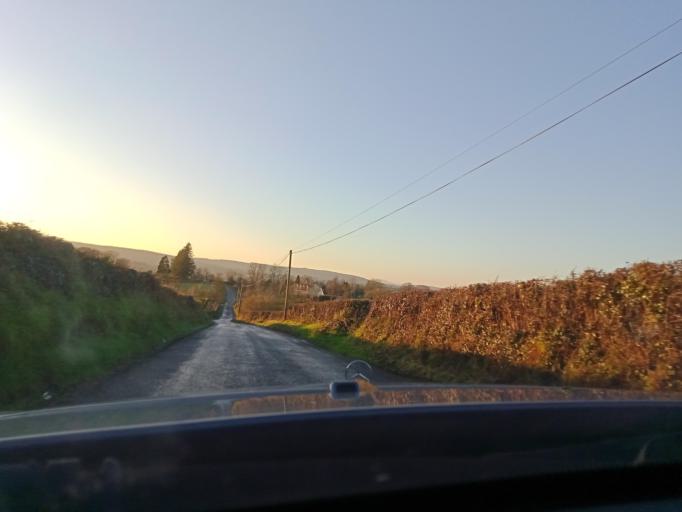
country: IE
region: Munster
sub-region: Waterford
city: Waterford
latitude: 52.3685
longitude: -7.1535
